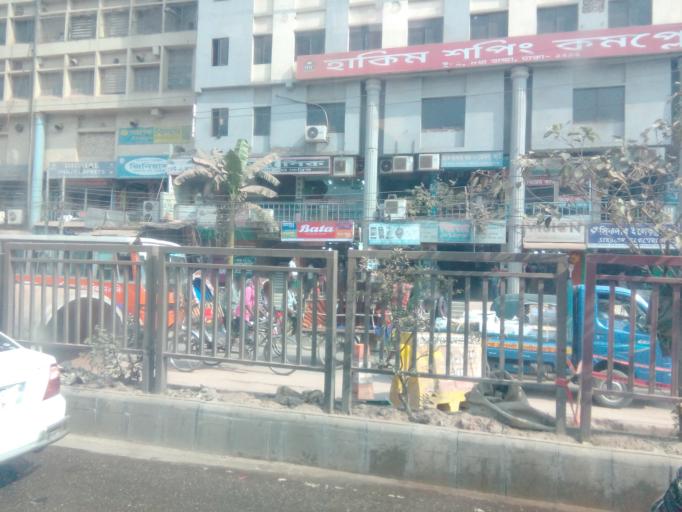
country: BD
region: Dhaka
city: Paltan
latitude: 23.7781
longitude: 90.4257
